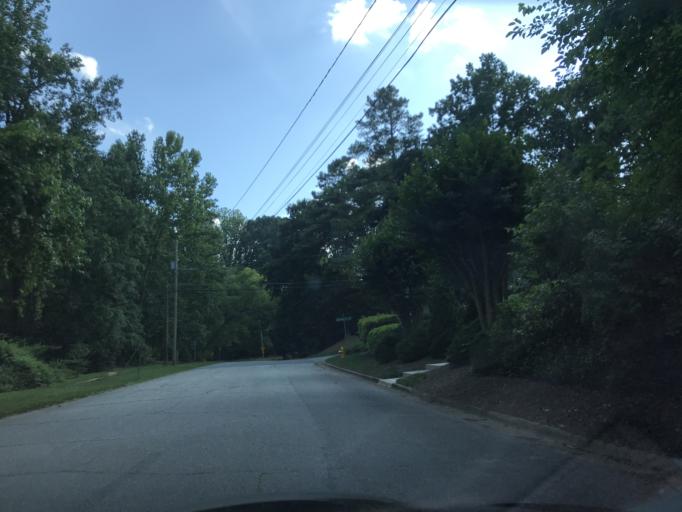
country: US
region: North Carolina
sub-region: Wake County
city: West Raleigh
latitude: 35.8121
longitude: -78.6728
